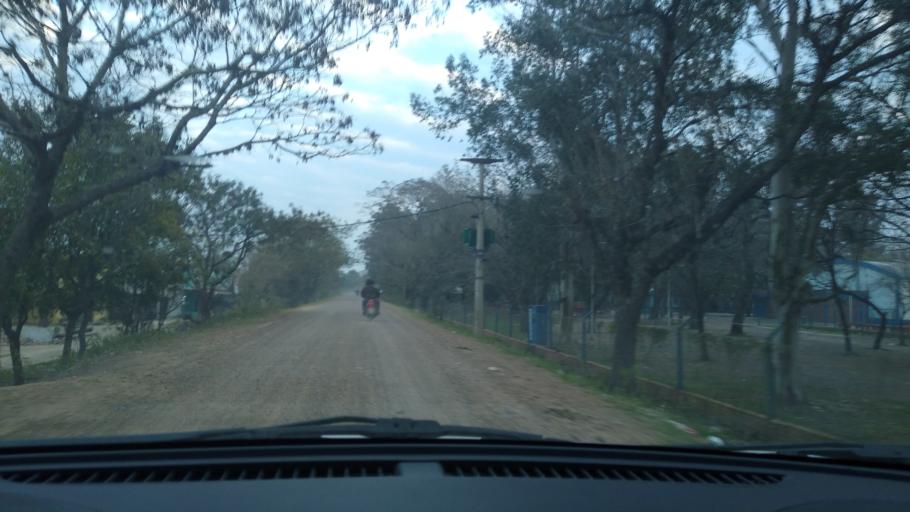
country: AR
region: Chaco
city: Barranqueras
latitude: -27.4616
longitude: -58.9460
